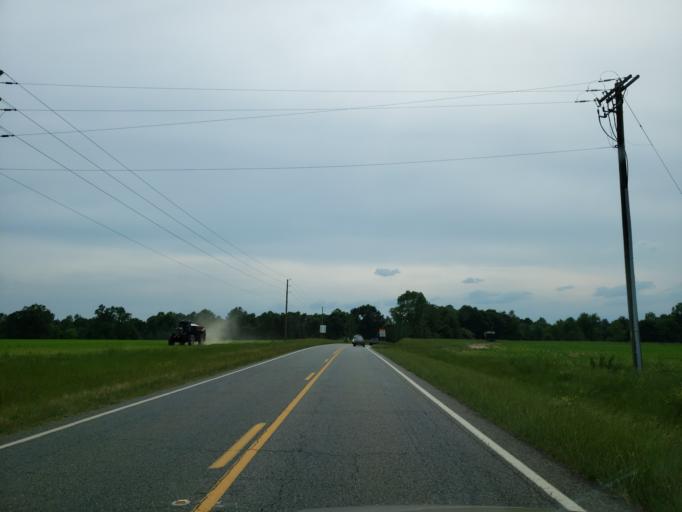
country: US
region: Georgia
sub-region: Macon County
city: Marshallville
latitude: 32.3671
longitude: -83.9029
